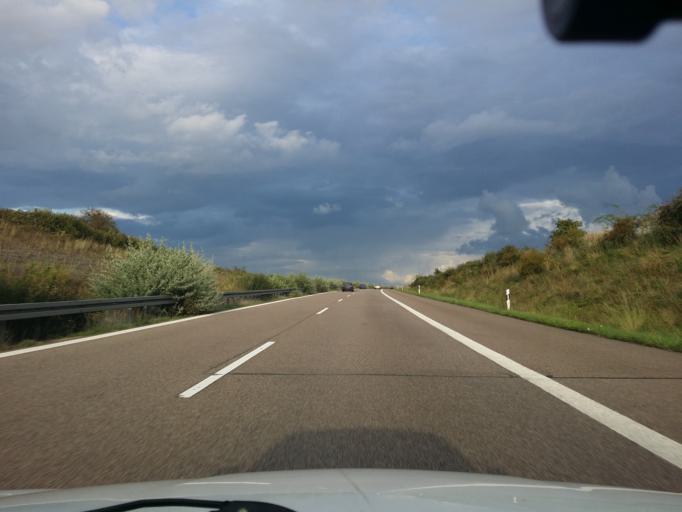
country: DE
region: Saxony-Anhalt
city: Wallhausen
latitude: 51.4629
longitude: 11.1700
